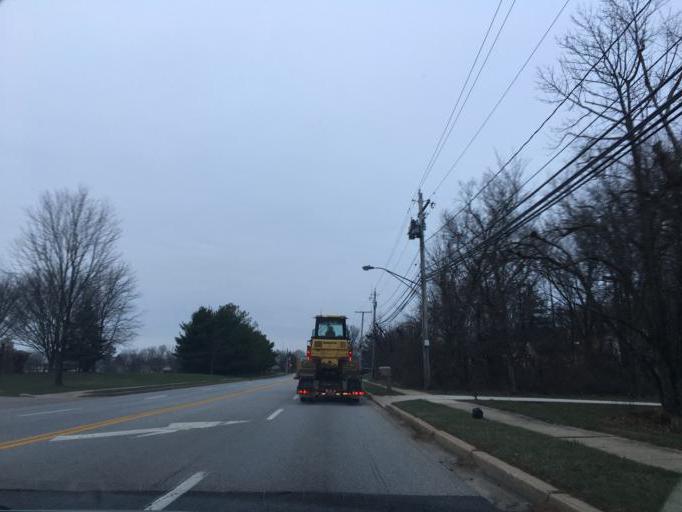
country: US
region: Maryland
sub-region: Baltimore County
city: Woodlawn
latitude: 39.3001
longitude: -76.7537
